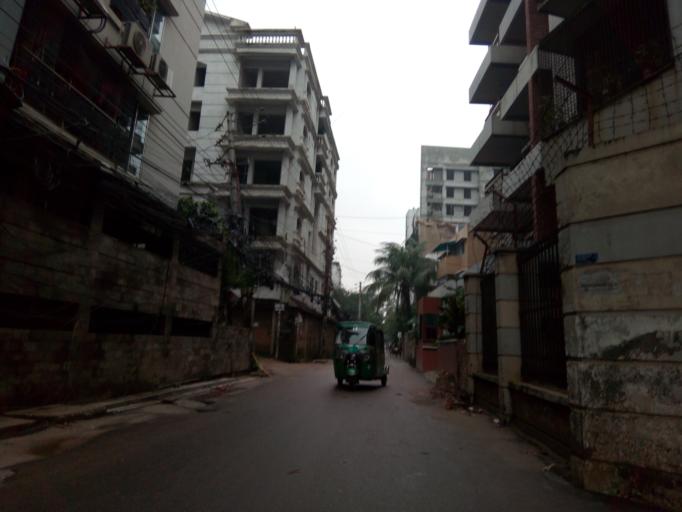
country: BD
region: Dhaka
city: Paltan
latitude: 23.7857
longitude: 90.4002
